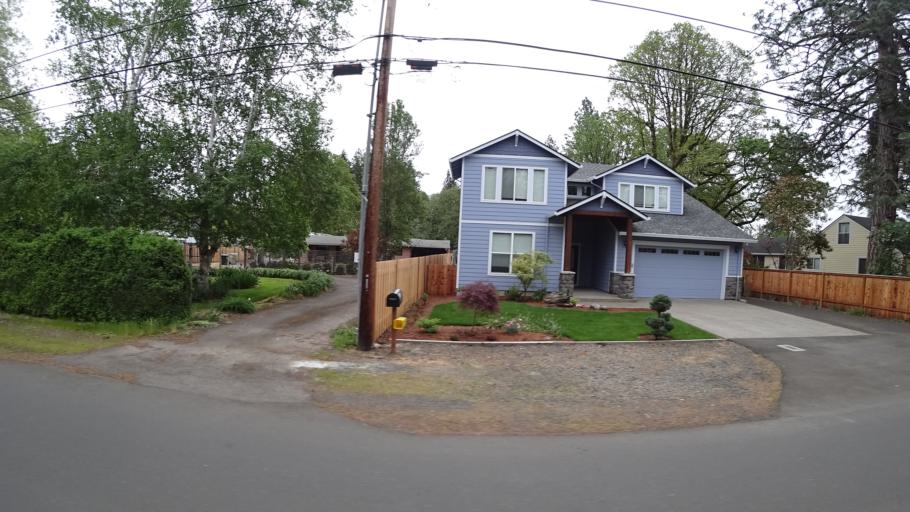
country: US
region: Oregon
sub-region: Washington County
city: Aloha
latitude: 45.5063
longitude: -122.8700
